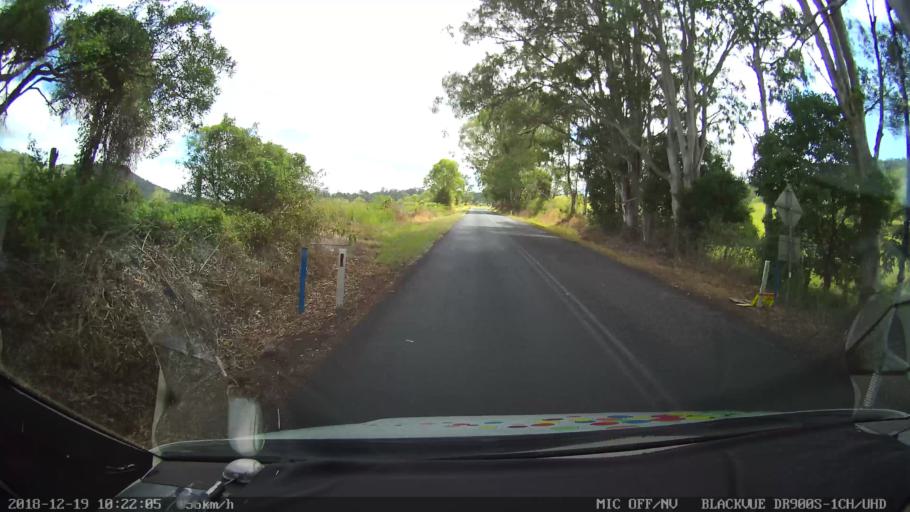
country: AU
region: New South Wales
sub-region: Kyogle
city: Kyogle
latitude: -28.5949
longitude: 153.0651
